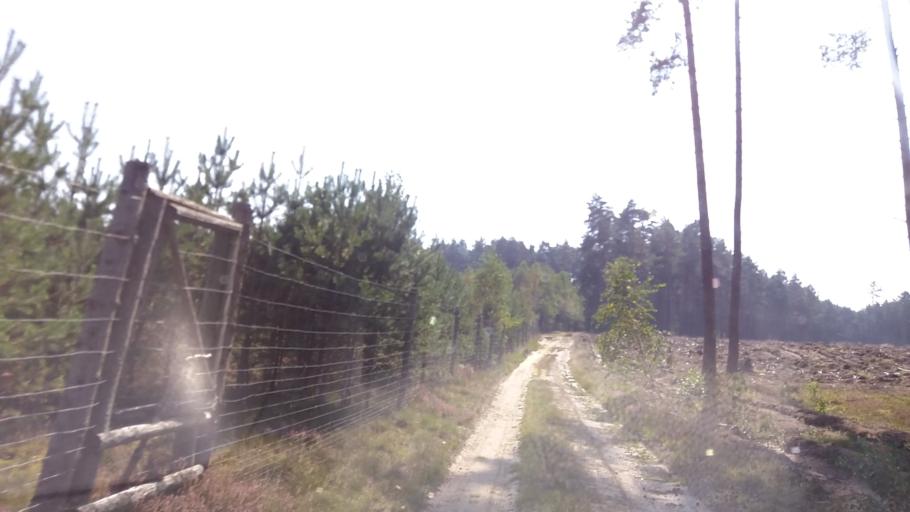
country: PL
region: West Pomeranian Voivodeship
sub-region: Powiat walecki
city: Miroslawiec
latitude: 53.2279
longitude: 16.0229
